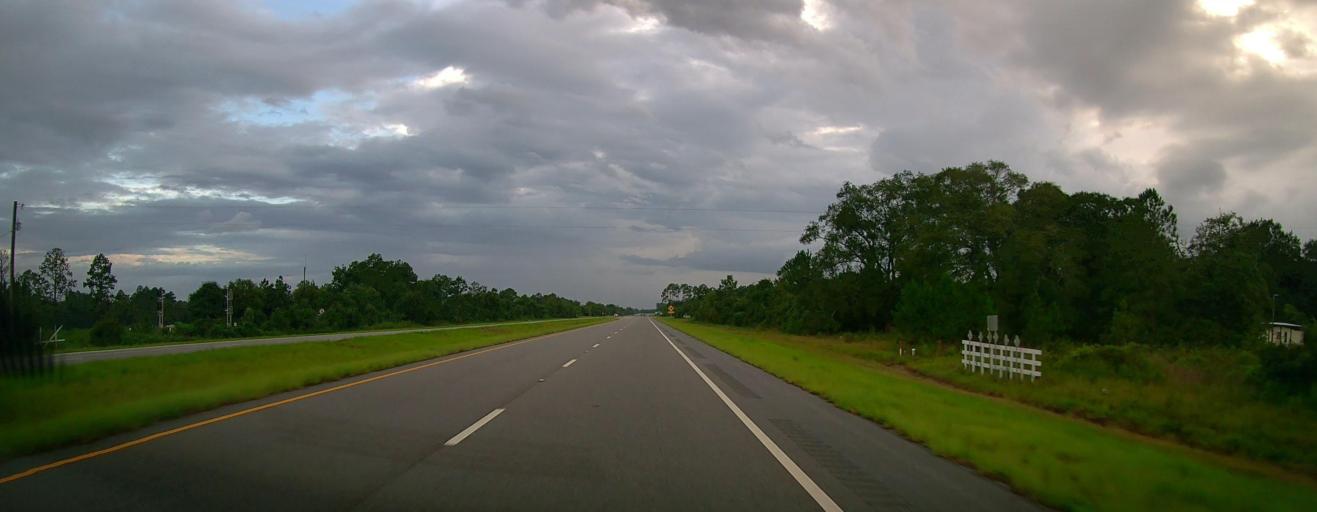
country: US
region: Georgia
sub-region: Ware County
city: Deenwood
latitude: 31.1583
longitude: -82.4265
